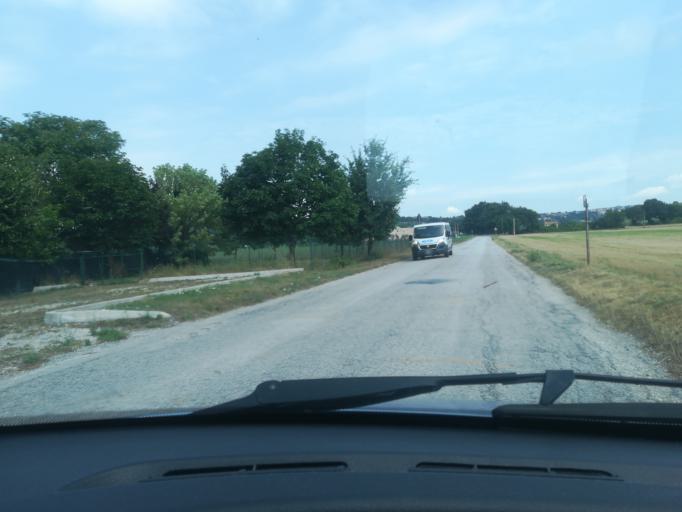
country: IT
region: The Marches
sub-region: Provincia di Macerata
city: Sforzacosta
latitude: 43.2665
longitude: 13.4390
